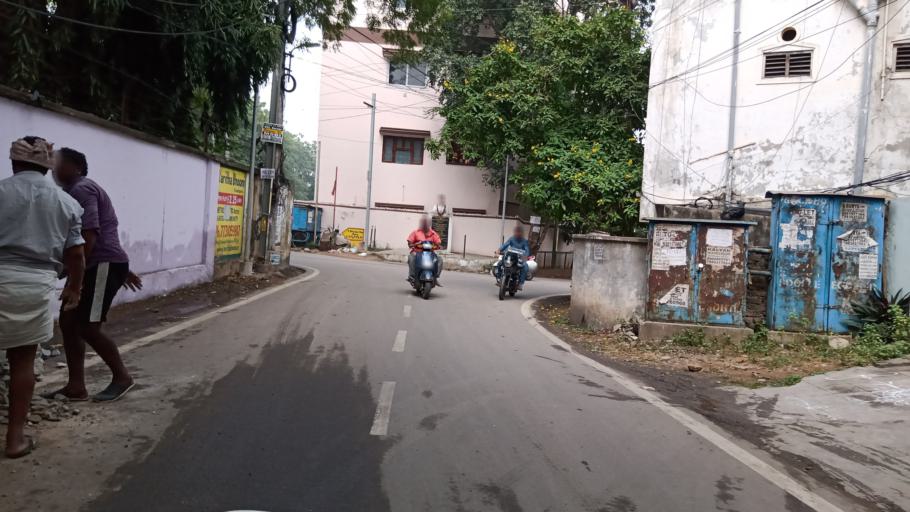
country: IN
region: Telangana
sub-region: Rangareddi
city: Kukatpalli
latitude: 17.4474
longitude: 78.4419
